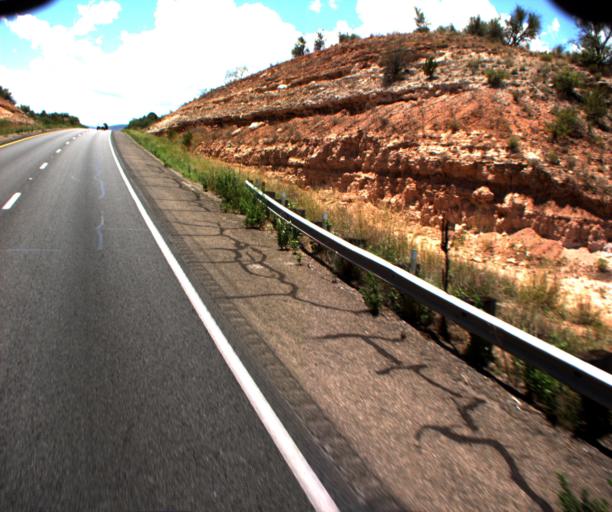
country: US
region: Arizona
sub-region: Yavapai County
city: Verde Village
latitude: 34.6753
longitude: -111.9719
